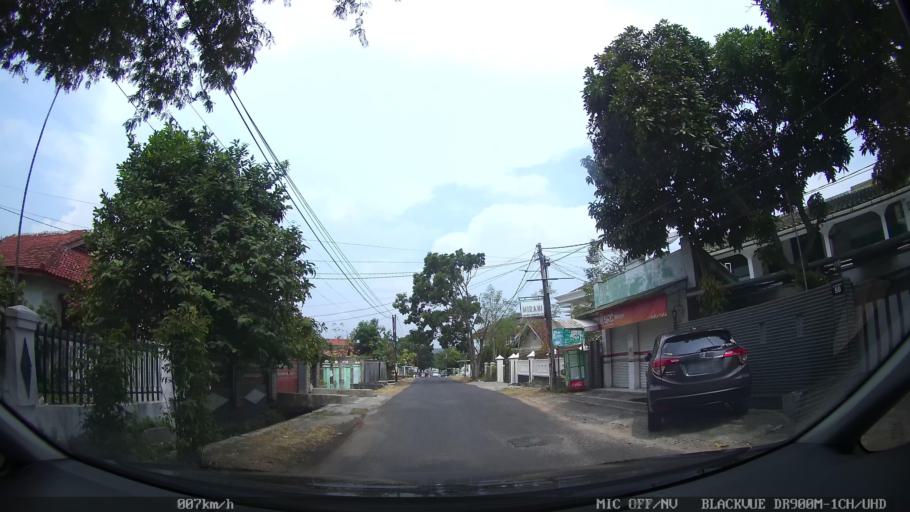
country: ID
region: Lampung
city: Bandarlampung
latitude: -5.4185
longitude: 105.2655
